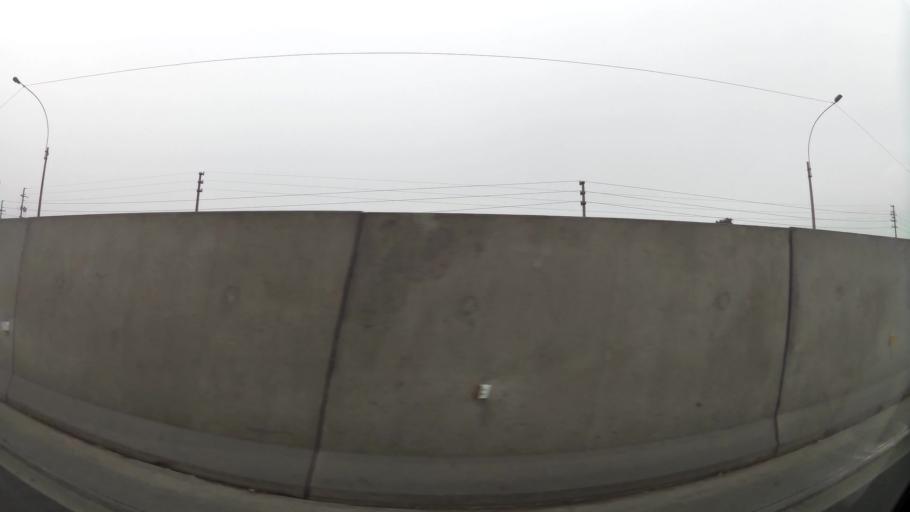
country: PE
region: Lima
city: Ventanilla
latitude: -11.8248
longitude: -77.1229
